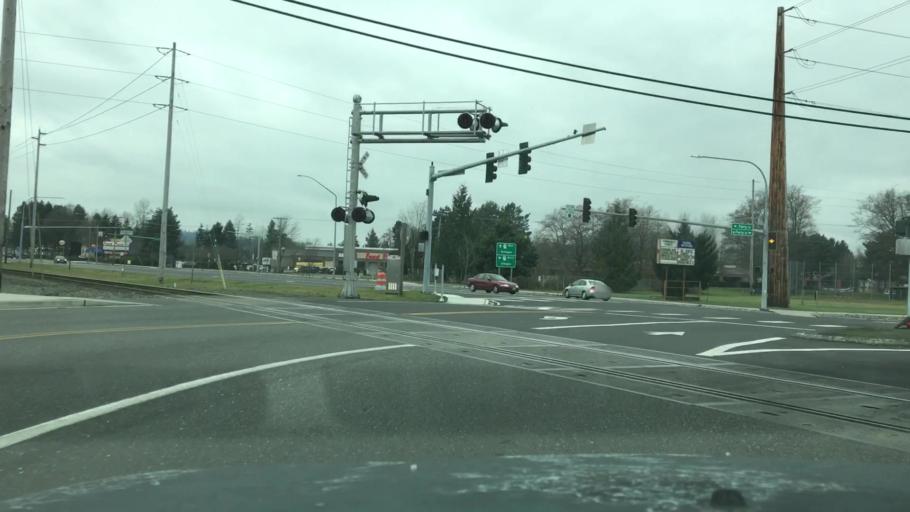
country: US
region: Washington
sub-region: Skagit County
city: Sedro-Woolley
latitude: 48.5054
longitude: -122.2452
